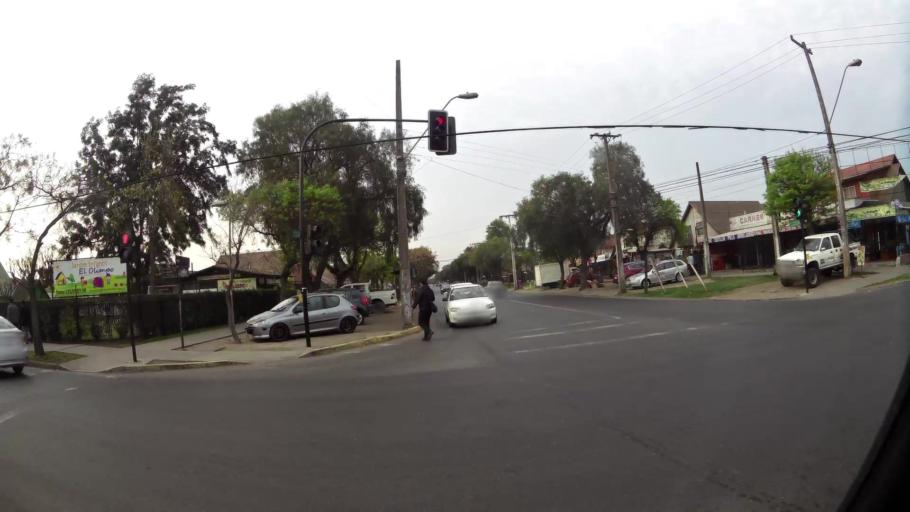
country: CL
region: Santiago Metropolitan
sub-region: Provincia de Santiago
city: Lo Prado
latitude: -33.5246
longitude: -70.7755
